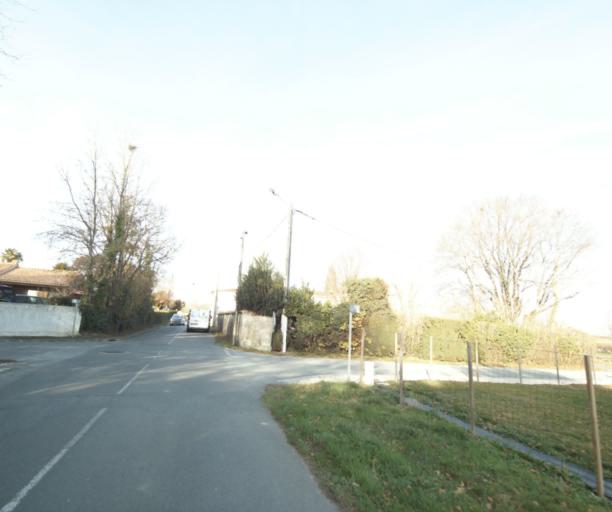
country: FR
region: Poitou-Charentes
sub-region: Departement de la Charente-Maritime
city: Chaniers
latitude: 45.7339
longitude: -0.5576
